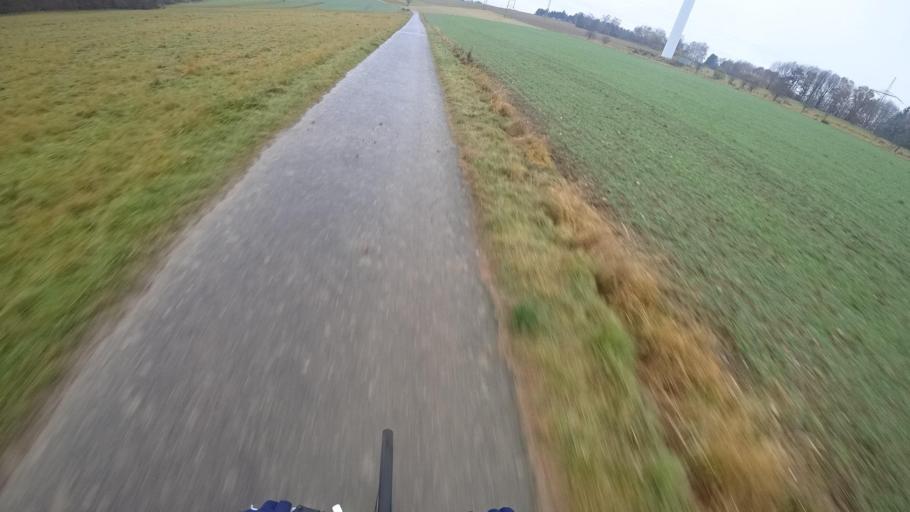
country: DE
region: Rheinland-Pfalz
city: Norath
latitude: 50.1306
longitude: 7.5898
